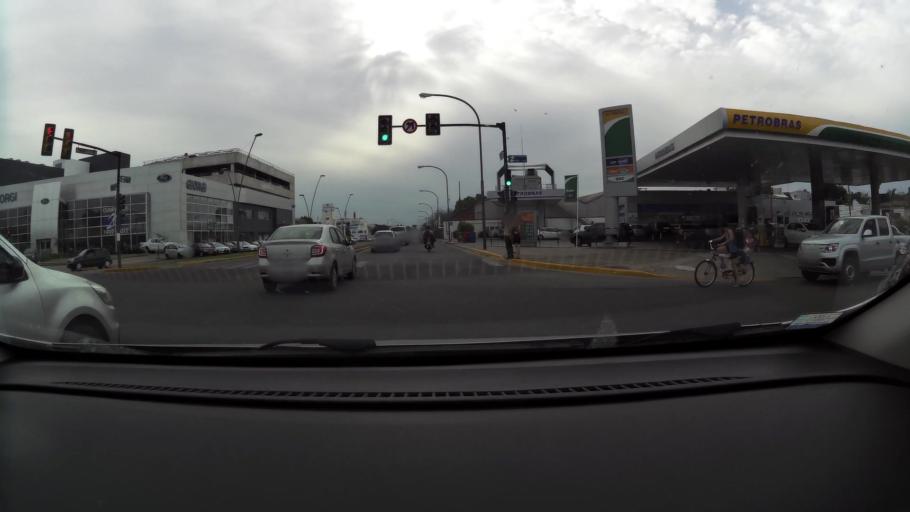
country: AR
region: Santa Fe
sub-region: Departamento de Rosario
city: Rosario
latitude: -32.9219
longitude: -60.6749
